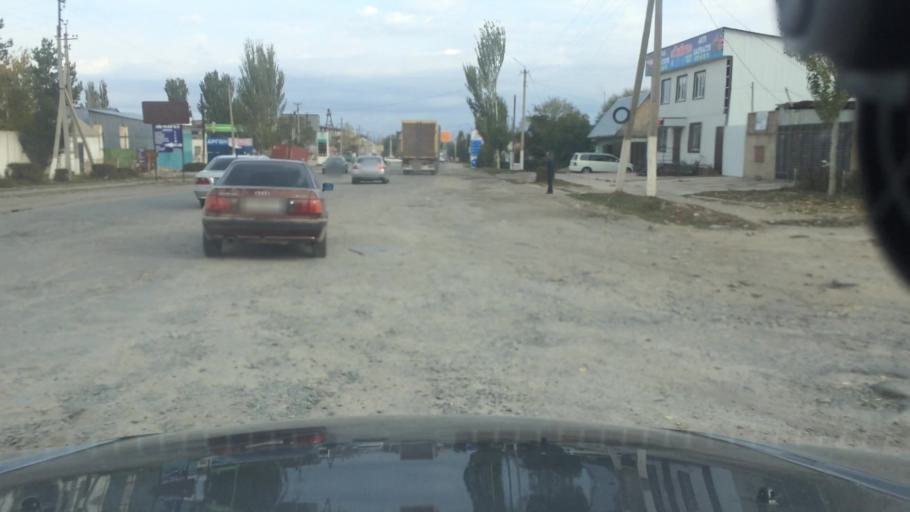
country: KG
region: Ysyk-Koel
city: Karakol
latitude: 42.5115
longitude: 78.3857
